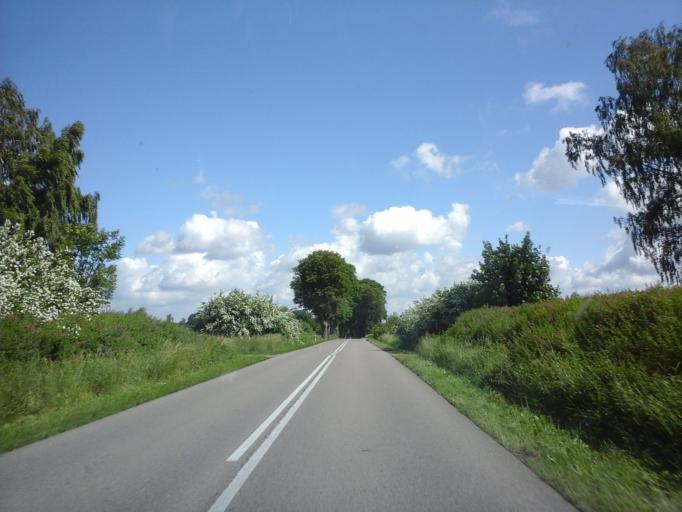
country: PL
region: West Pomeranian Voivodeship
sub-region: Powiat lobeski
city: Wegorzyno
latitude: 53.5787
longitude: 15.5906
